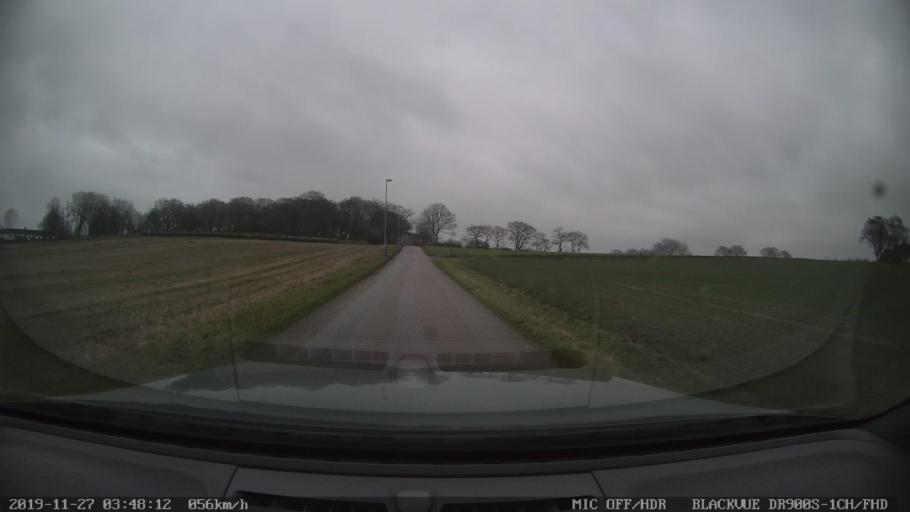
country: SE
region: Skane
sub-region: Hoganas Kommun
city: Hoganas
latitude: 56.2603
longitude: 12.5658
